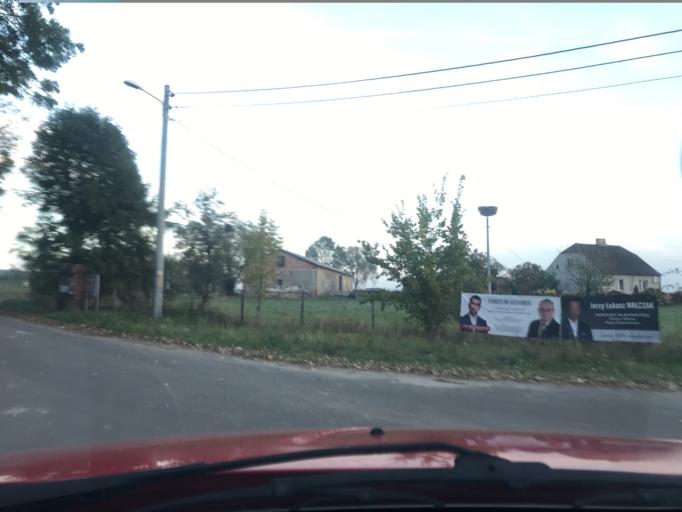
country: PL
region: Greater Poland Voivodeship
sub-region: Powiat ostrowski
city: Skalmierzyce
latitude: 51.7557
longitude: 17.9031
